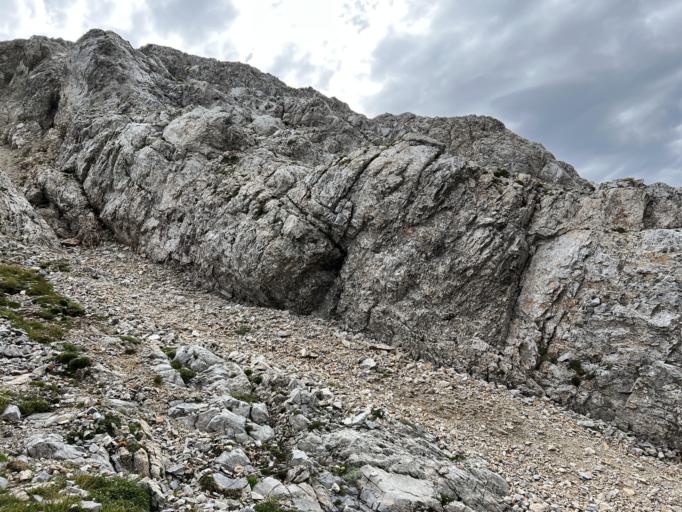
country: IT
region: Friuli Venezia Giulia
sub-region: Provincia di Udine
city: Forni Avoltri
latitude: 46.6288
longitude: 12.8174
